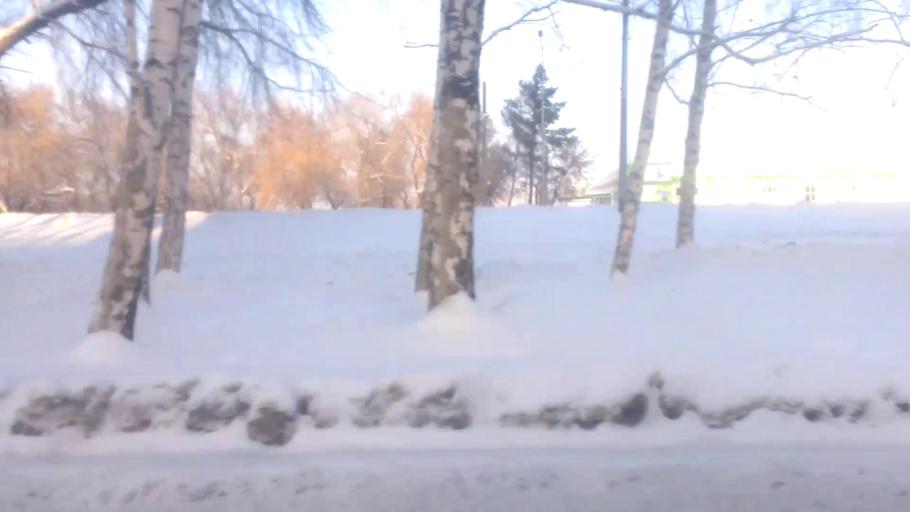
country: RU
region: Altai Krai
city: Novosilikatnyy
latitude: 53.3459
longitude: 83.6529
